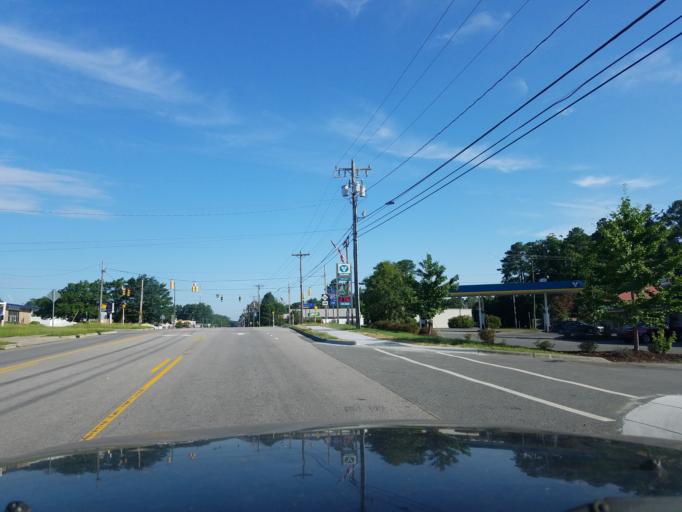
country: US
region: North Carolina
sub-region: Granville County
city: Butner
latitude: 36.1328
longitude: -78.7572
